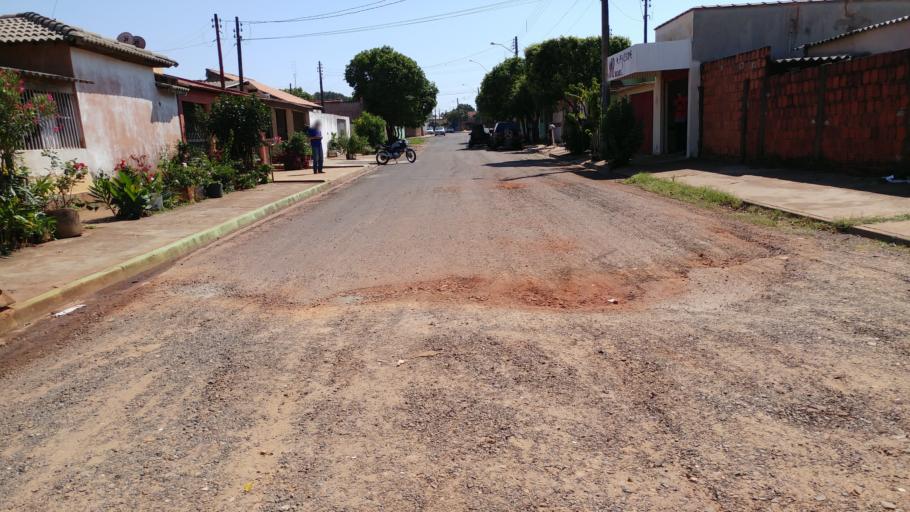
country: BR
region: Sao Paulo
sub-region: Paraguacu Paulista
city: Paraguacu Paulista
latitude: -22.4214
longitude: -50.5890
